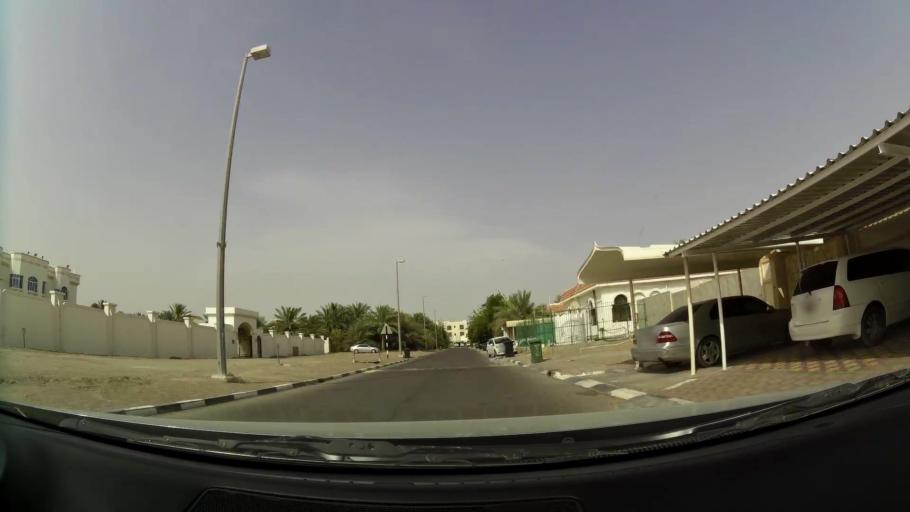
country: AE
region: Abu Dhabi
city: Al Ain
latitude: 24.1865
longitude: 55.6127
